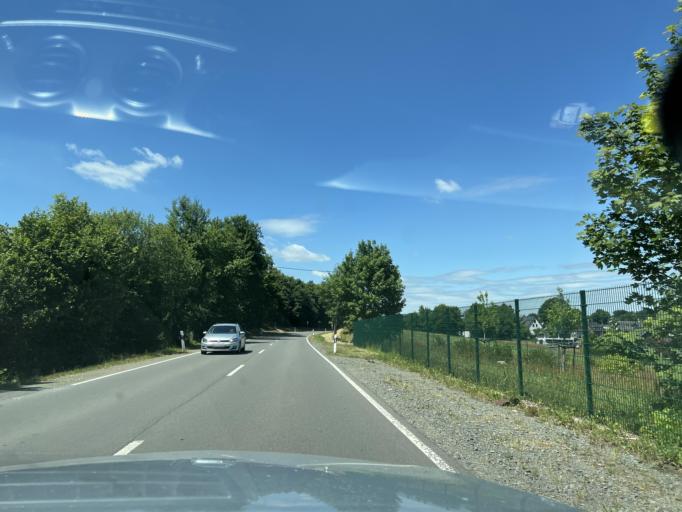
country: DE
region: North Rhine-Westphalia
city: Freudenberg
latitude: 50.9351
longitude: 7.9021
